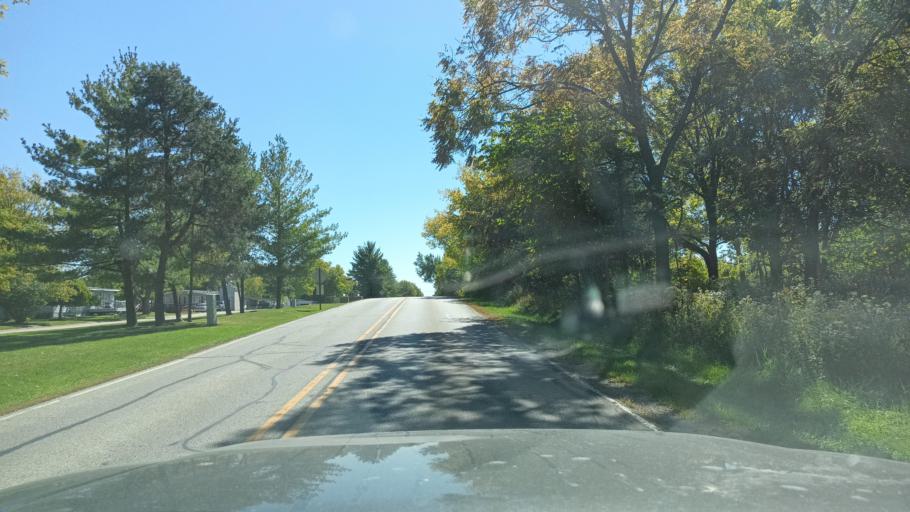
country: US
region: Illinois
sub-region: Champaign County
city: Lake of the Woods
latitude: 40.2104
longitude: -88.3654
